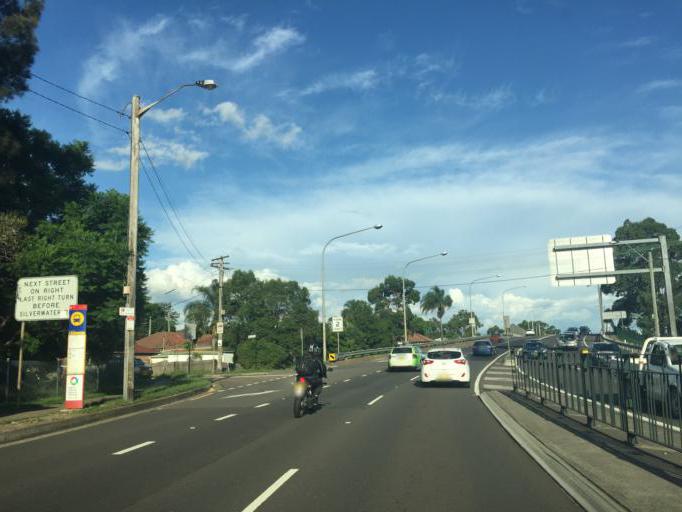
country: AU
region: New South Wales
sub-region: Parramatta
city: Telopea
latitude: -33.8090
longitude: 151.0280
